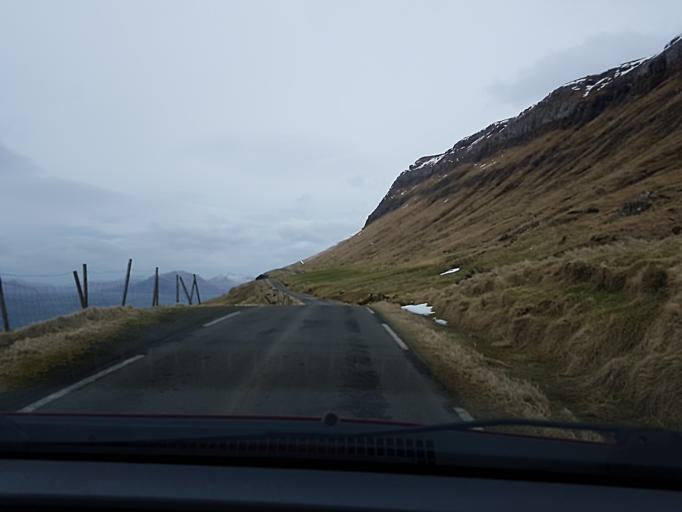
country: FO
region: Streymoy
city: Hoyvik
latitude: 61.9899
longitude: -6.8762
